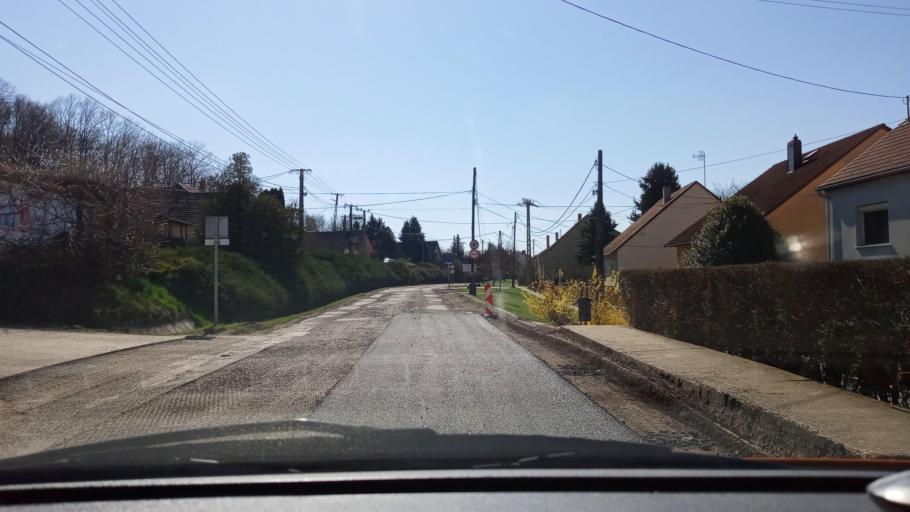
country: HU
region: Baranya
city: Boly
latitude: 46.0155
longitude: 18.4109
